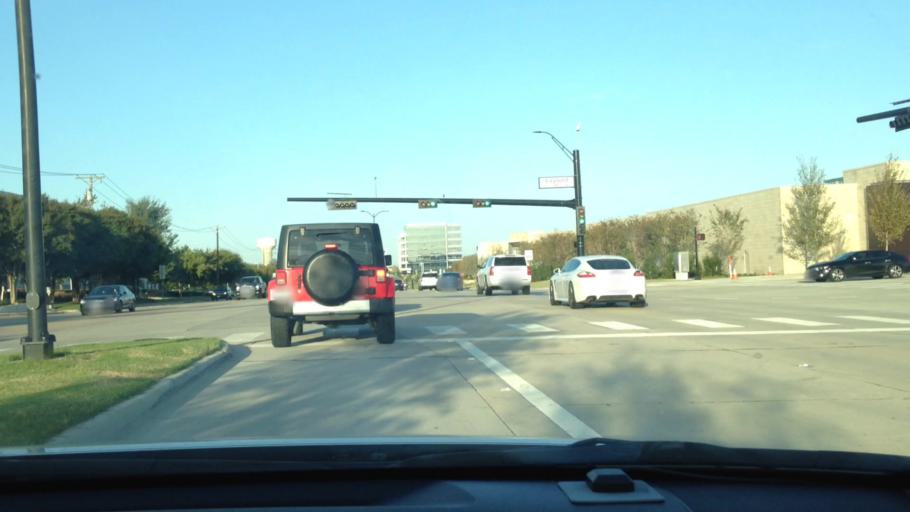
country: US
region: Texas
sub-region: Collin County
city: Frisco
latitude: 33.1068
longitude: -96.8259
